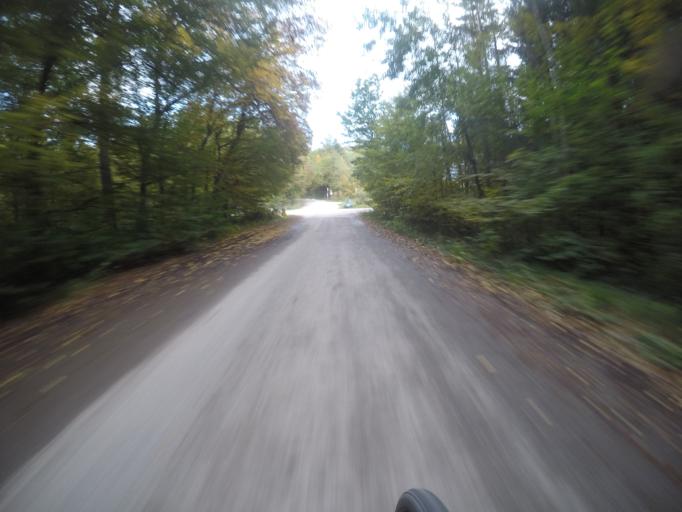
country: DE
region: Baden-Wuerttemberg
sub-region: Regierungsbezirk Stuttgart
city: Schonaich
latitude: 48.6873
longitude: 9.0627
